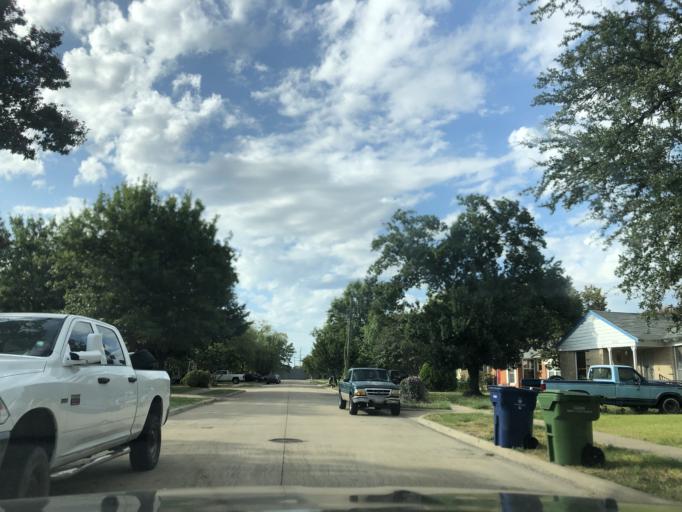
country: US
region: Texas
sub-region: Dallas County
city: Garland
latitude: 32.8805
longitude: -96.6638
